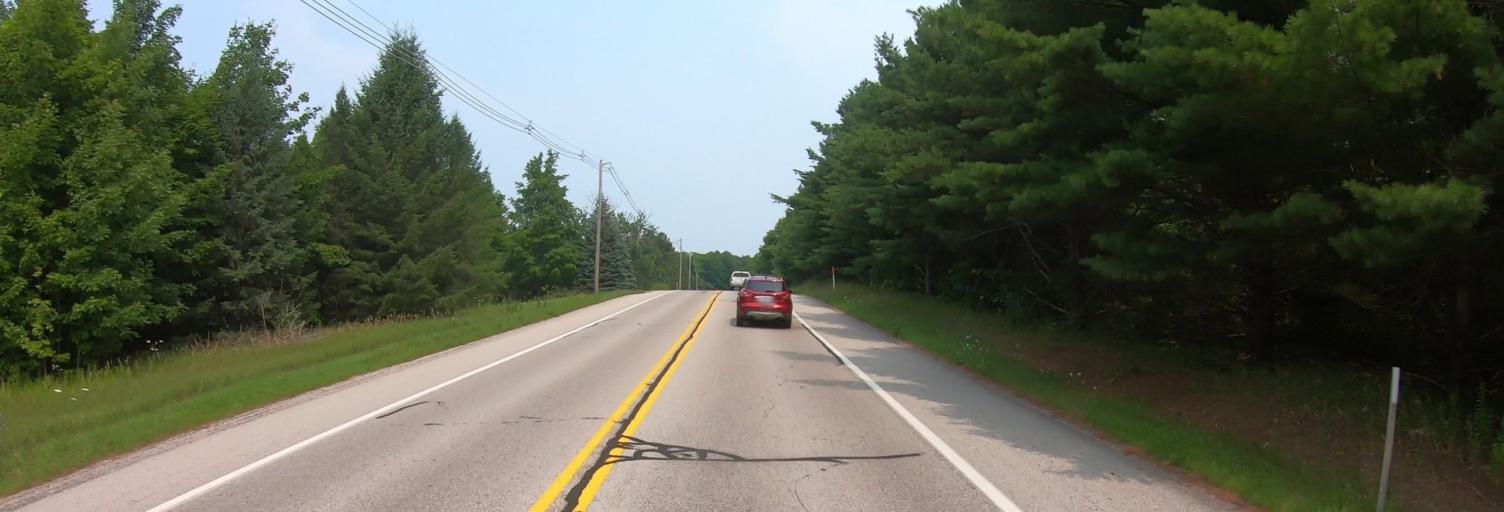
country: US
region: Michigan
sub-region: Leelanau County
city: Leland
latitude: 45.1011
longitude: -85.6471
